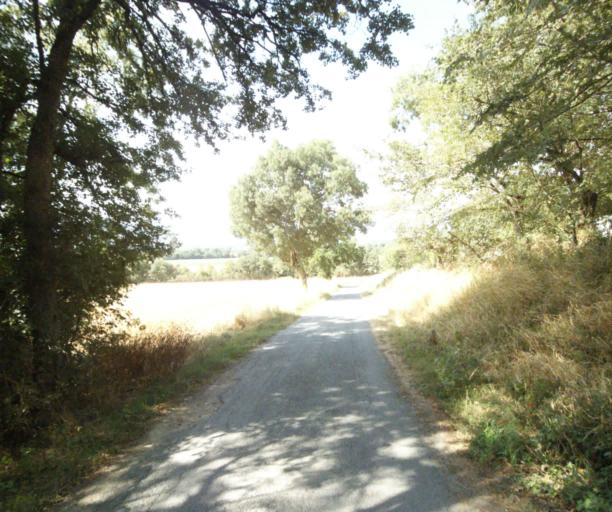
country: FR
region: Midi-Pyrenees
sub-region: Departement du Tarn
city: Puylaurens
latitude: 43.5139
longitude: 2.0367
